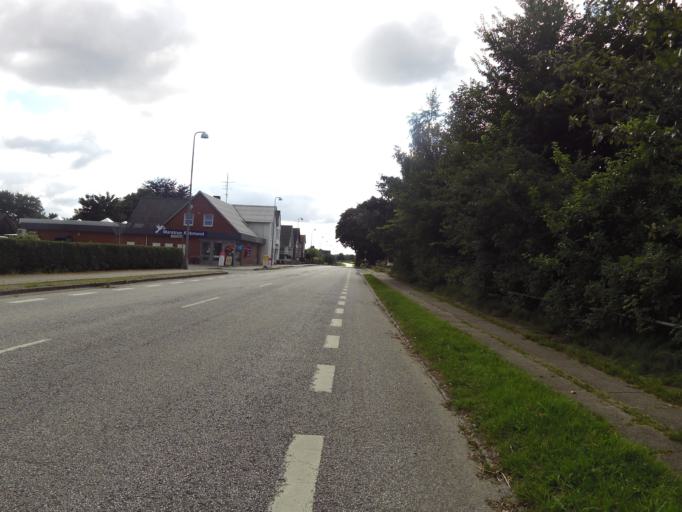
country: DK
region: South Denmark
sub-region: Haderslev Kommune
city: Haderslev
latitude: 55.2083
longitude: 9.4427
